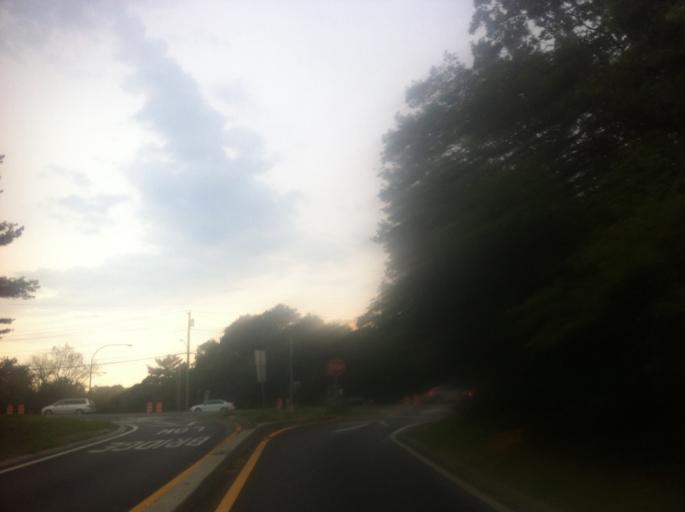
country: US
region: New York
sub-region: Nassau County
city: Jericho
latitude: 40.7887
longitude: -73.5208
